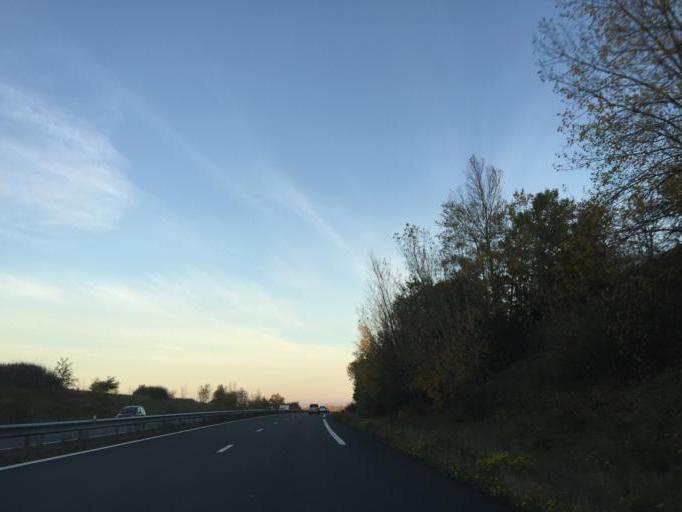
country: FR
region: Rhone-Alpes
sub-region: Departement de la Loire
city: Commelle-Vernay
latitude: 45.9823
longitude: 4.1190
